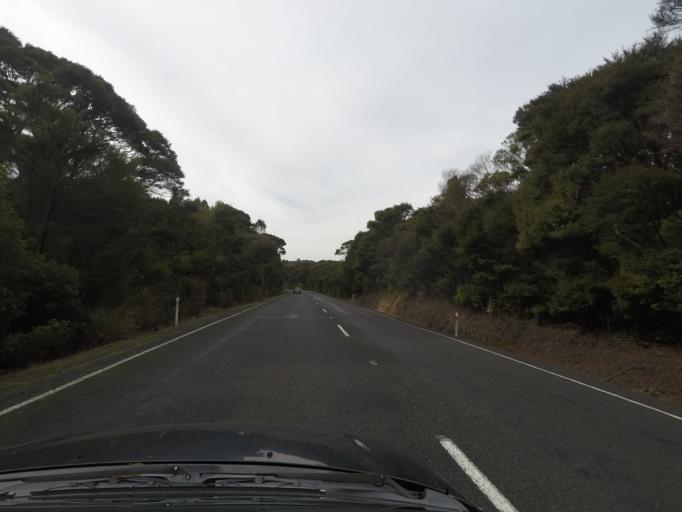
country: NZ
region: Auckland
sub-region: Auckland
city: Titirangi
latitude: -36.9427
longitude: 174.5509
